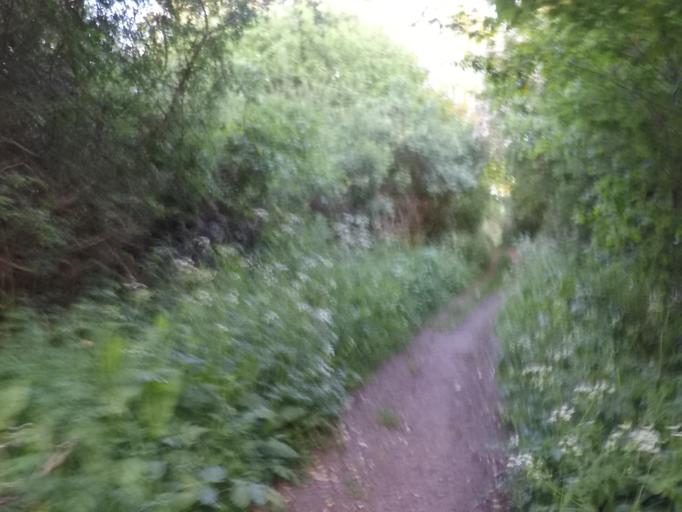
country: GB
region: England
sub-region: Oxfordshire
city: Charlbury
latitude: 51.8293
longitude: -1.5071
